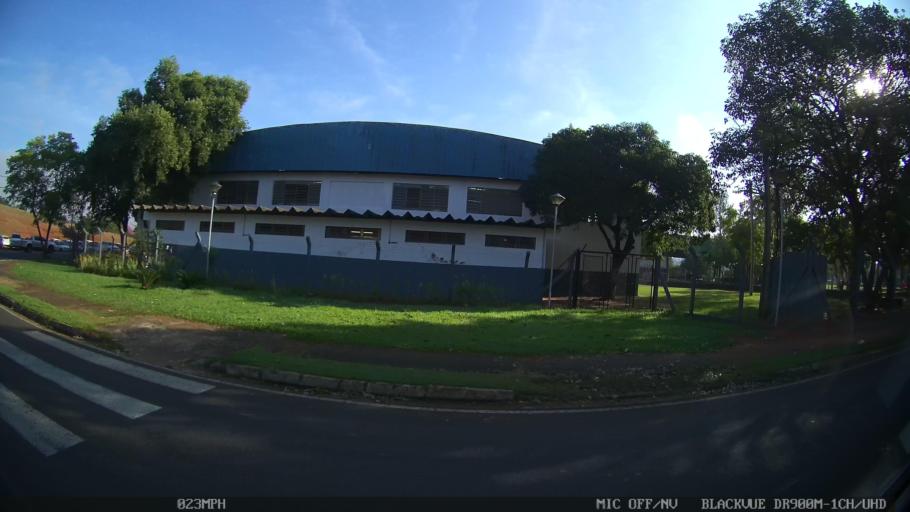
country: BR
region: Sao Paulo
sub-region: Sao Jose Do Rio Preto
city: Sao Jose do Rio Preto
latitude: -20.8110
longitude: -49.3660
